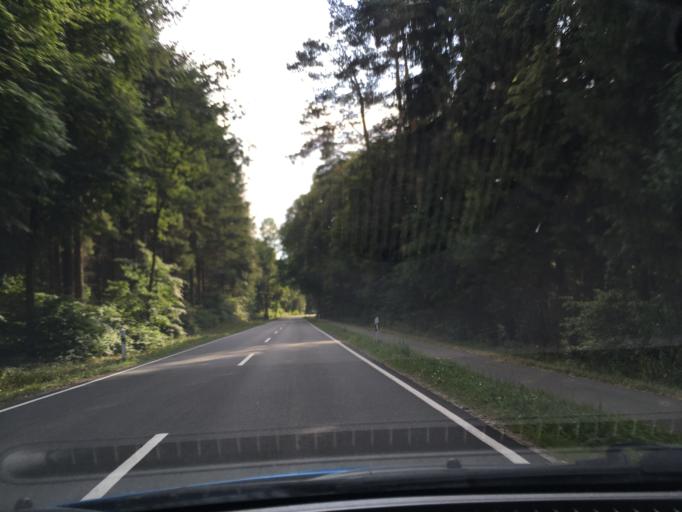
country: DE
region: Lower Saxony
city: Karwitz
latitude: 53.0765
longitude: 10.9616
